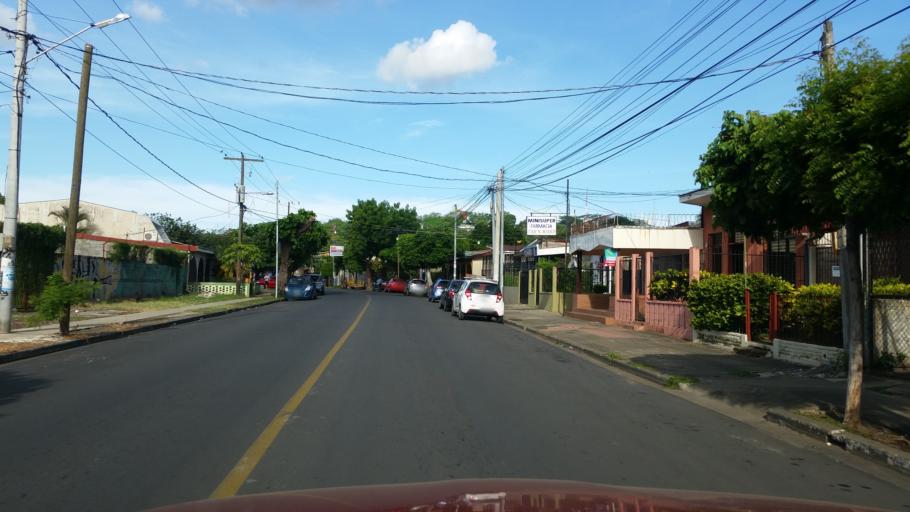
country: NI
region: Managua
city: Managua
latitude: 12.1418
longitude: -86.2798
